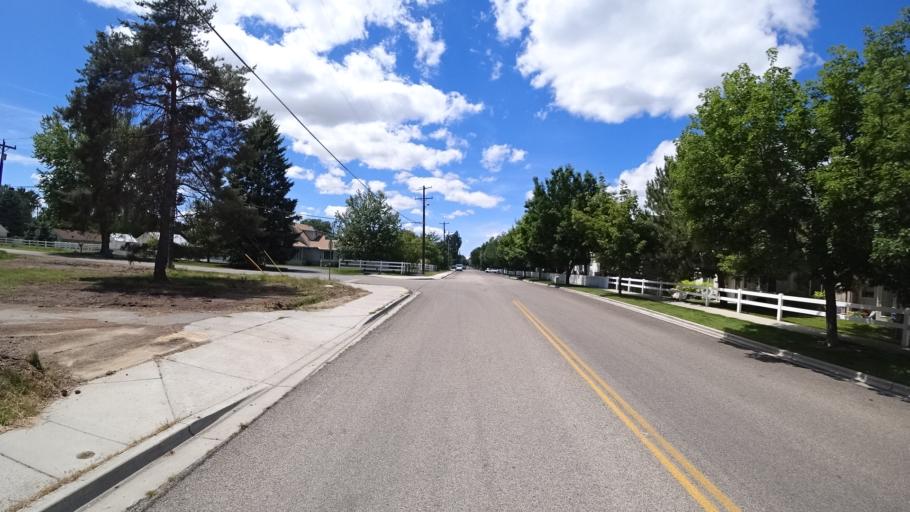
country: US
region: Idaho
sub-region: Ada County
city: Boise
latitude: 43.5945
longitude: -116.1844
